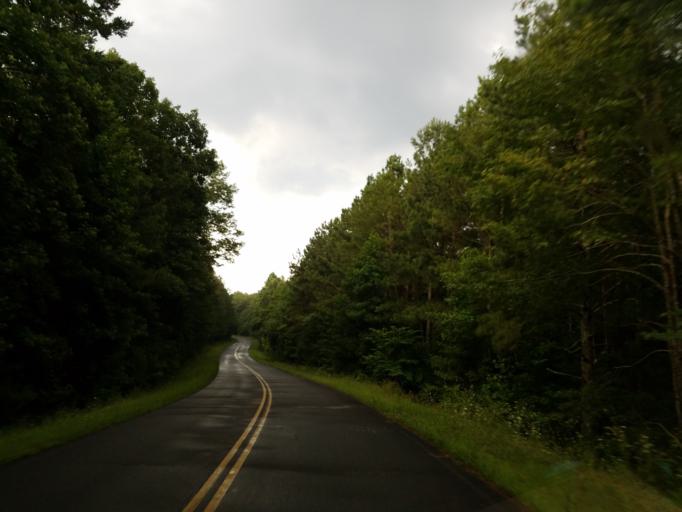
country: US
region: Georgia
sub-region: Whitfield County
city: Dalton
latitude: 34.6467
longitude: -85.0903
